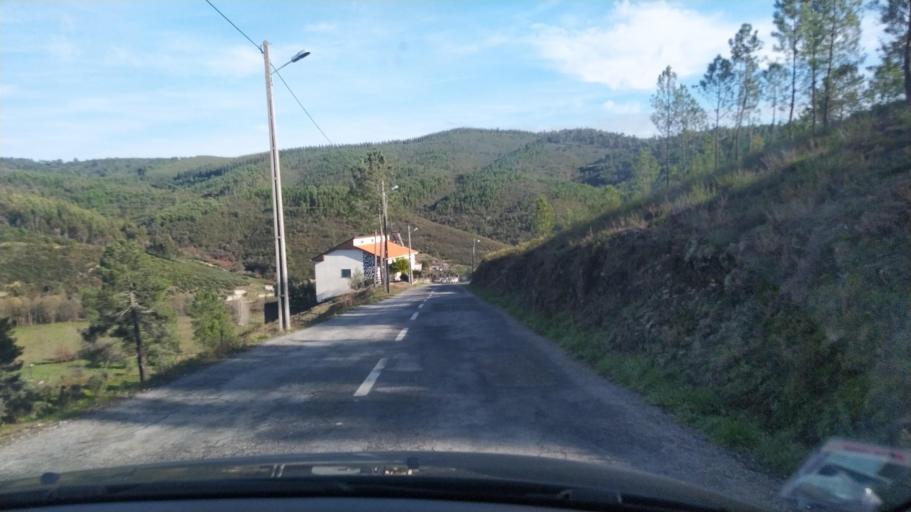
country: PT
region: Castelo Branco
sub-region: Concelho do Fundao
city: Aldeia de Joanes
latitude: 40.1822
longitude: -7.6970
